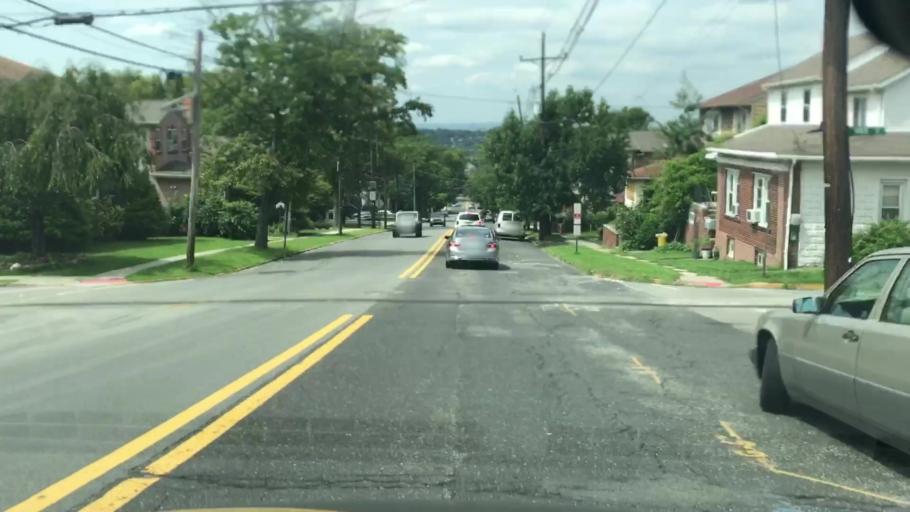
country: US
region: New Jersey
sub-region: Bergen County
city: Palisades Park
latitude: 40.8435
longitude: -73.9894
